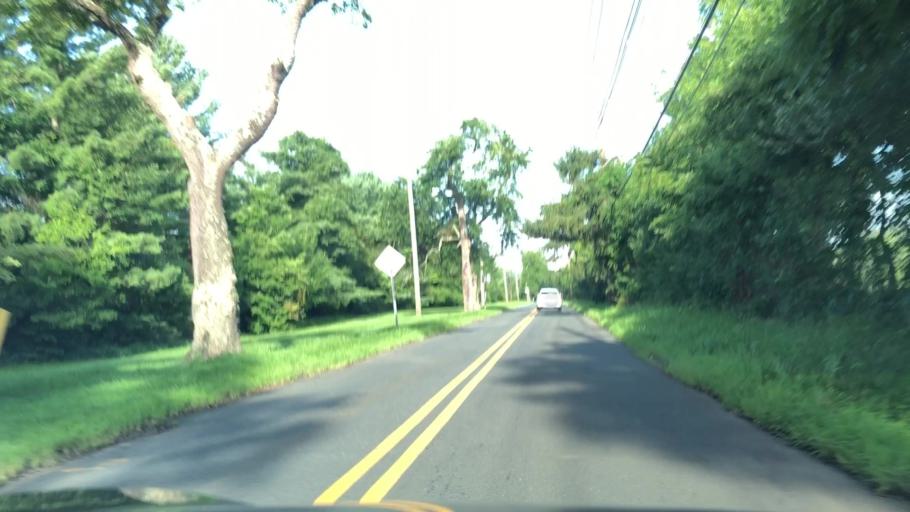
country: US
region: New Jersey
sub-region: Mercer County
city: Pennington
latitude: 40.3495
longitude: -74.7672
